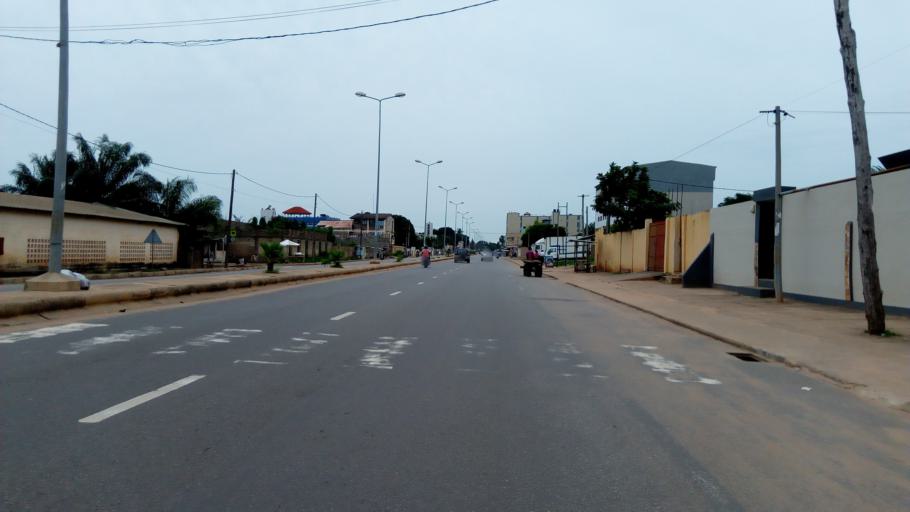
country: TG
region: Maritime
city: Lome
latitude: 6.1613
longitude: 1.2323
